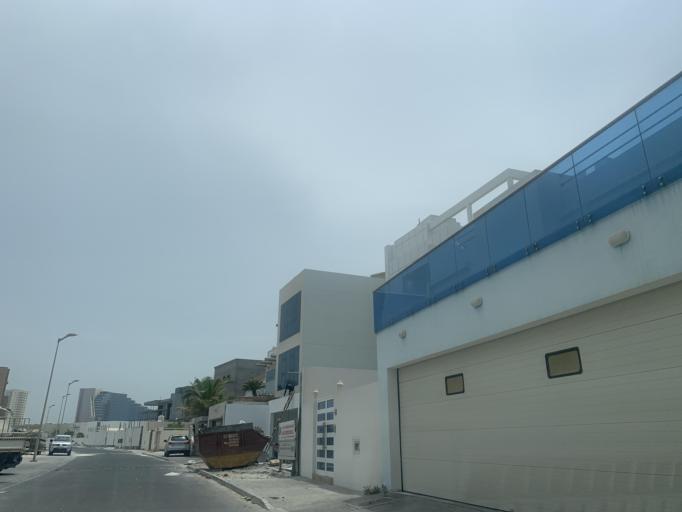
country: BH
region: Muharraq
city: Al Hadd
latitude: 26.2962
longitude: 50.6576
